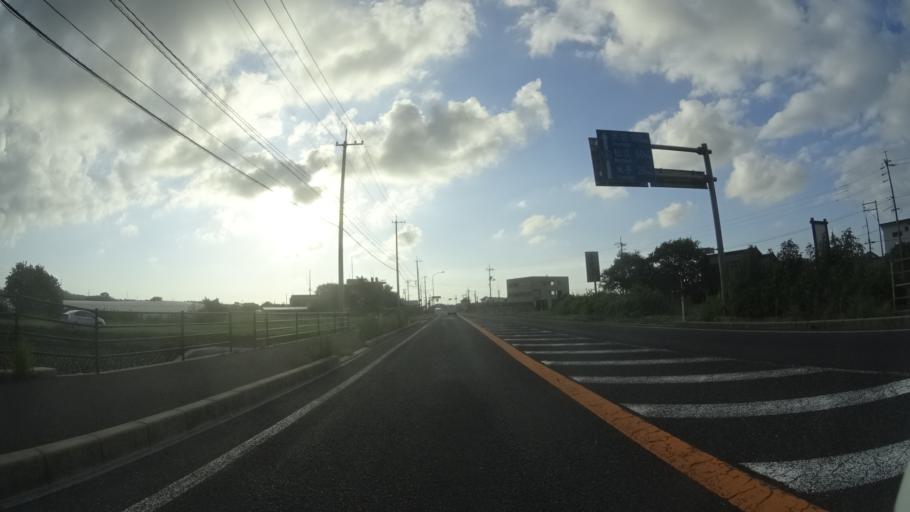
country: JP
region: Tottori
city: Kurayoshi
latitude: 35.5243
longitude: 133.5868
